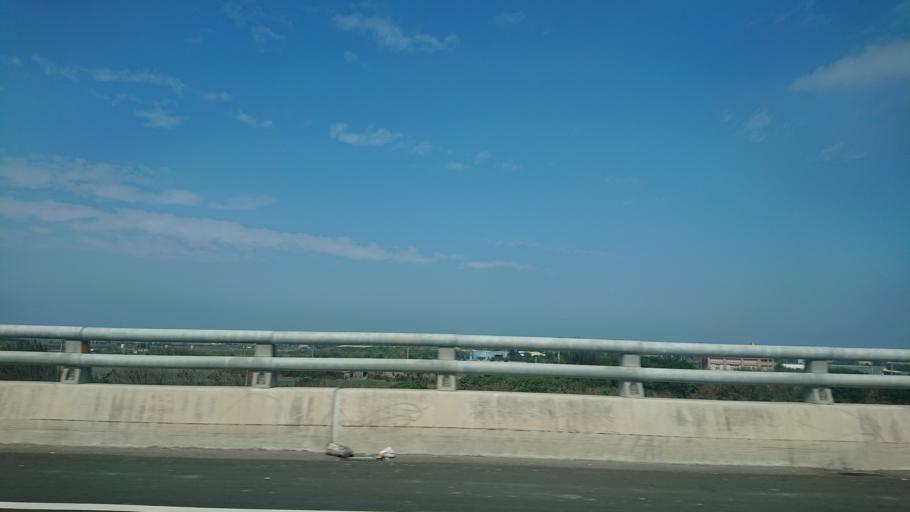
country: TW
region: Taiwan
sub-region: Changhua
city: Chang-hua
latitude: 23.9895
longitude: 120.3715
